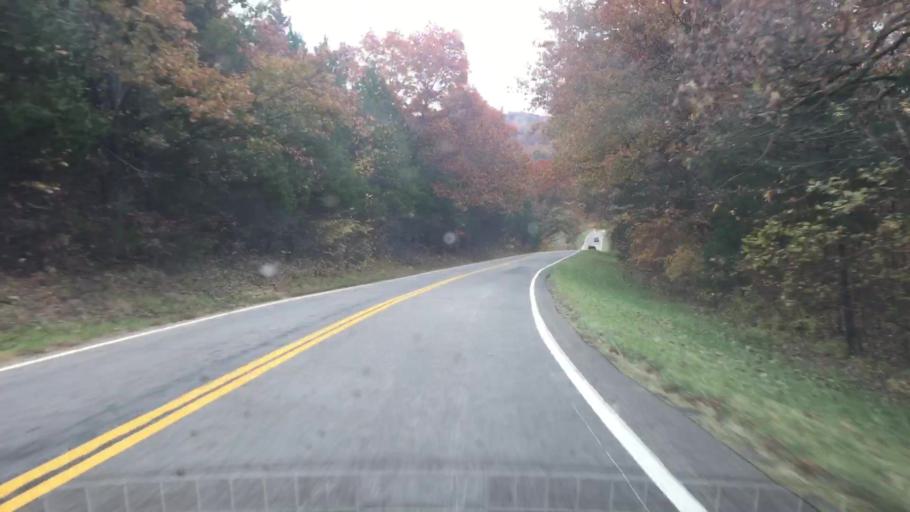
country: US
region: Missouri
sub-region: Gasconade County
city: Hermann
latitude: 38.7090
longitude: -91.6291
